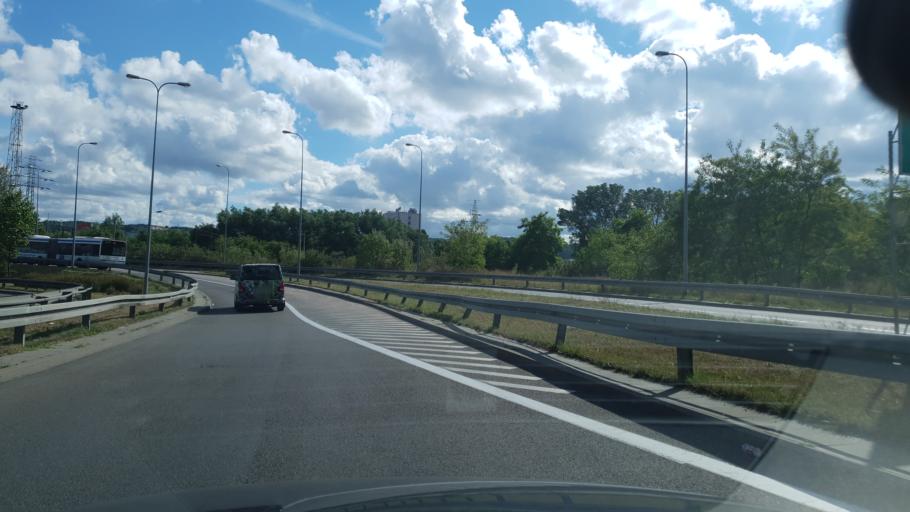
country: PL
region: Pomeranian Voivodeship
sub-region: Gdynia
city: Pogorze
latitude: 54.5424
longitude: 18.4958
